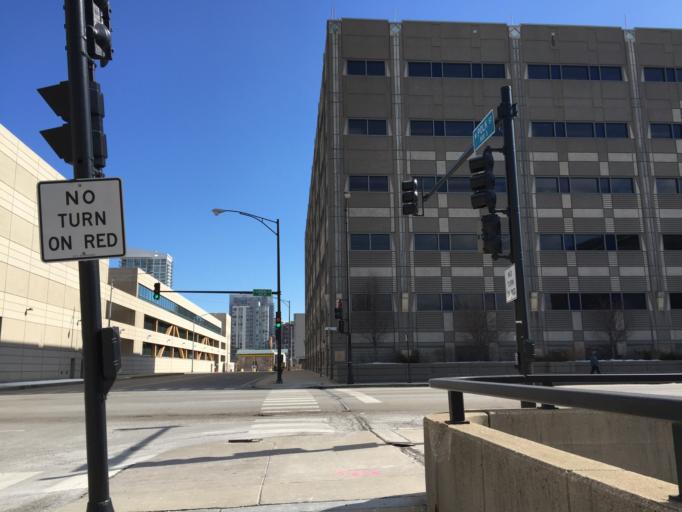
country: US
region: Illinois
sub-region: Cook County
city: Chicago
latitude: 41.8723
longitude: -87.6399
